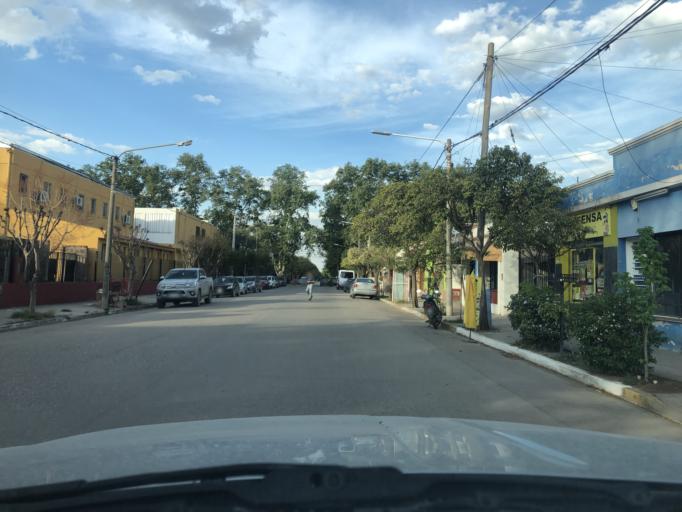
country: AR
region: Cordoba
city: Jesus Maria
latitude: -31.0215
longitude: -64.0631
